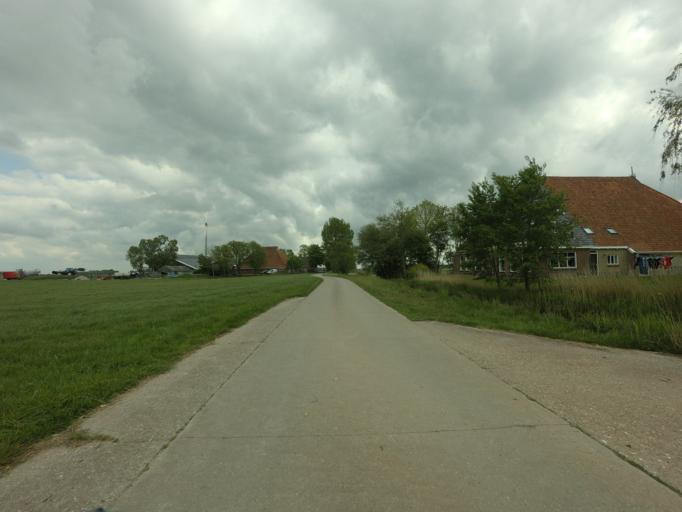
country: NL
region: Friesland
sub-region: Gemeente Littenseradiel
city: Wommels
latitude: 53.1096
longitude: 5.6127
